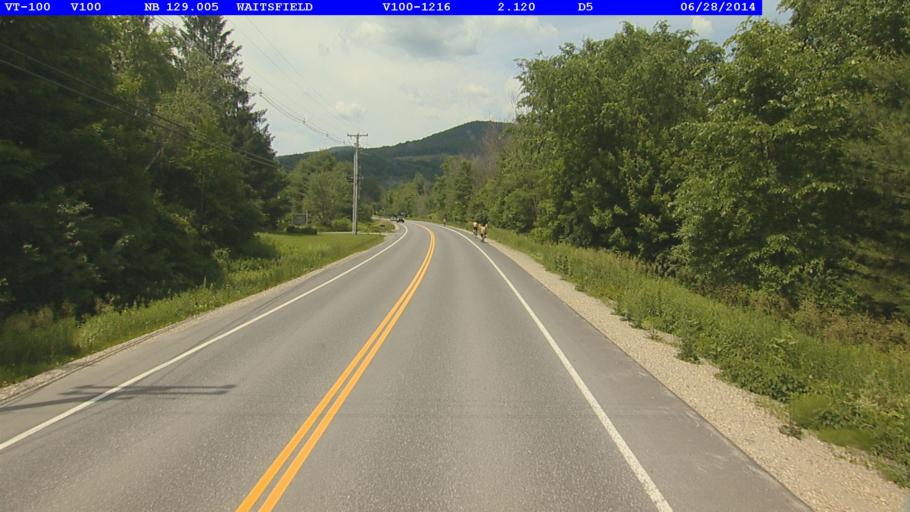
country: US
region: Vermont
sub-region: Washington County
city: Northfield
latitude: 44.1758
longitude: -72.8338
